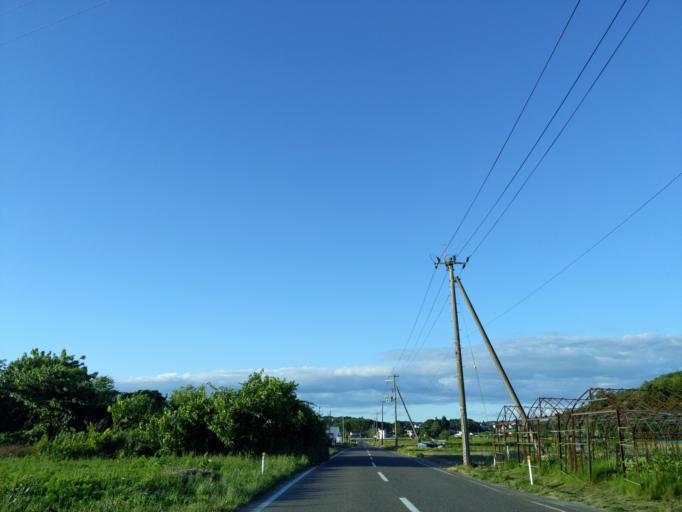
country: JP
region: Fukushima
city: Koriyama
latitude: 37.4142
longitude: 140.4142
